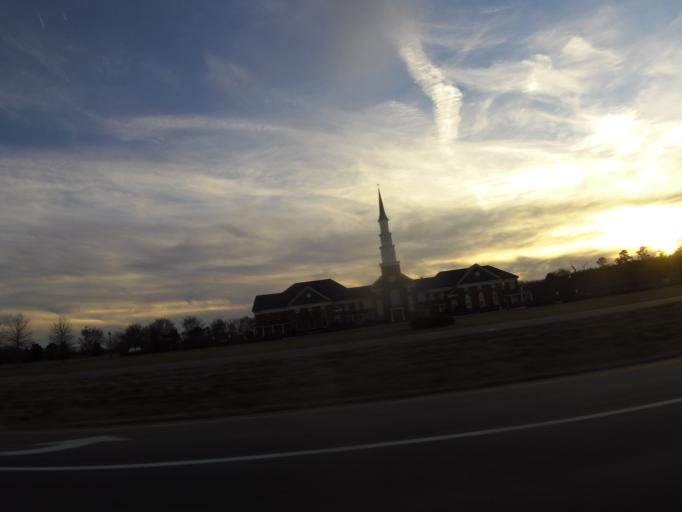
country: US
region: Virginia
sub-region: City of Franklin
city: Franklin
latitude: 36.6887
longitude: -76.9779
